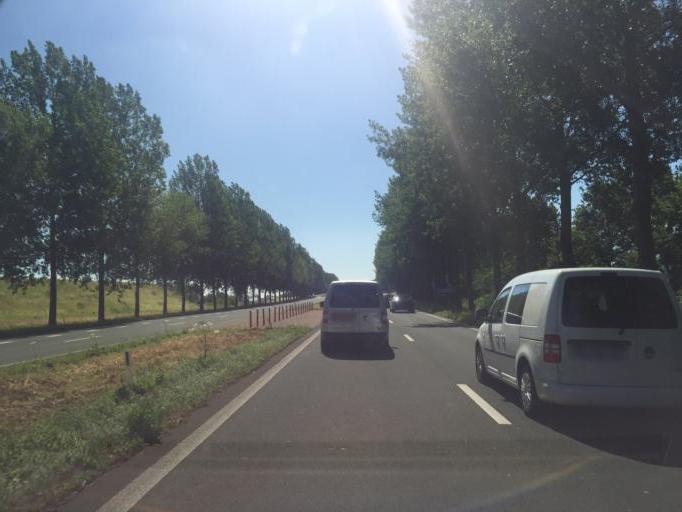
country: NL
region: North Holland
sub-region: Gemeente Haarlemmermeer
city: Hoofddorp
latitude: 52.3158
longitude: 4.6958
